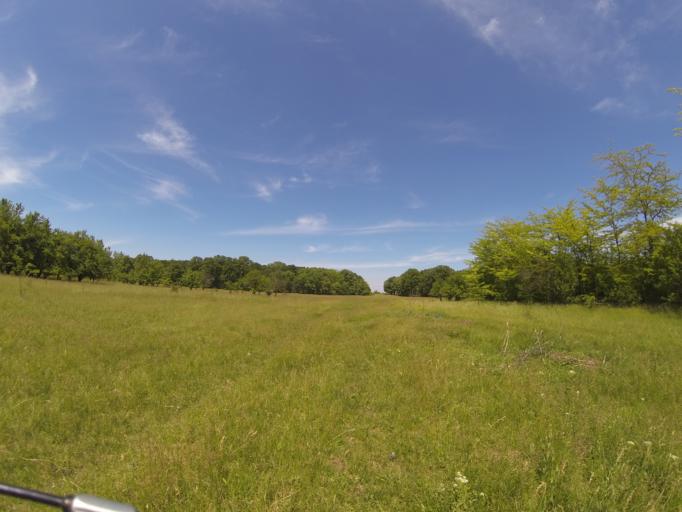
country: RO
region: Dolj
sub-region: Comuna Teslui
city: Teslui
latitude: 44.1723
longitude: 24.1664
